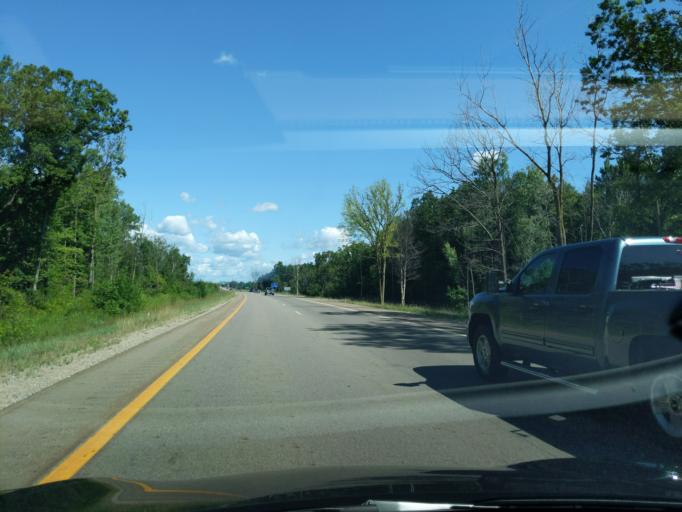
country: US
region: Michigan
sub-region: Gratiot County
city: Saint Louis
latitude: 43.3687
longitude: -84.6004
